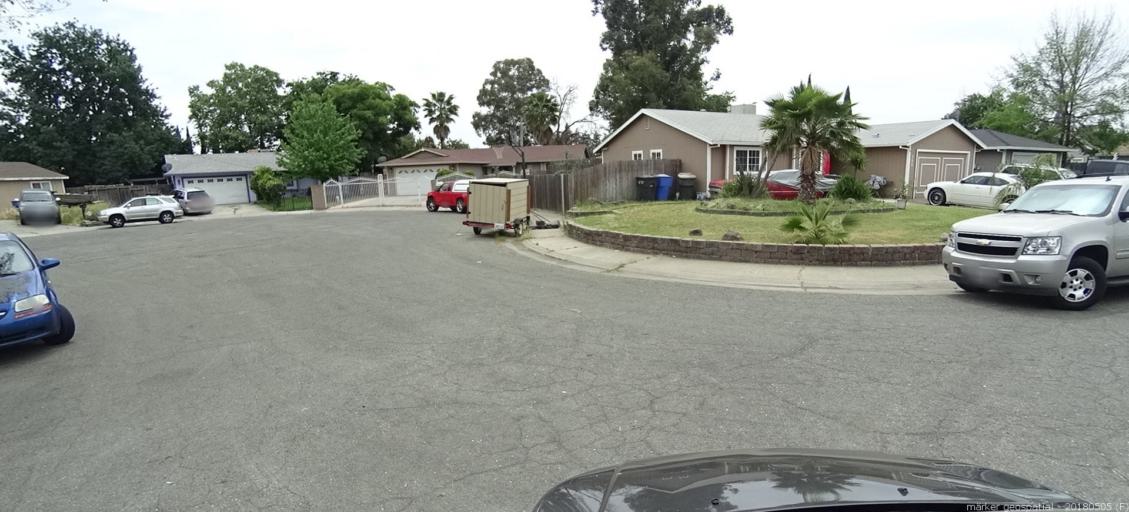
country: US
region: California
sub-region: Sacramento County
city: Rio Linda
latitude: 38.6427
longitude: -121.4592
